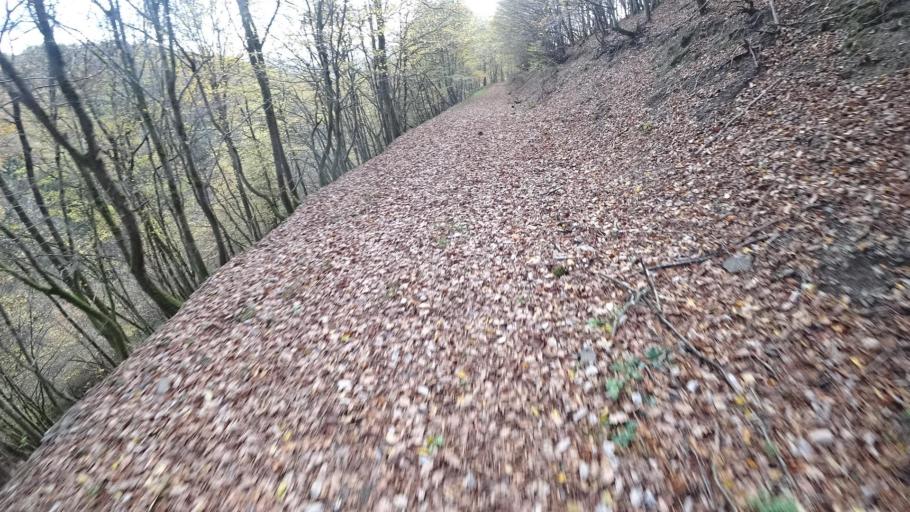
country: DE
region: Rheinland-Pfalz
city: Lind
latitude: 50.4867
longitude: 6.9181
